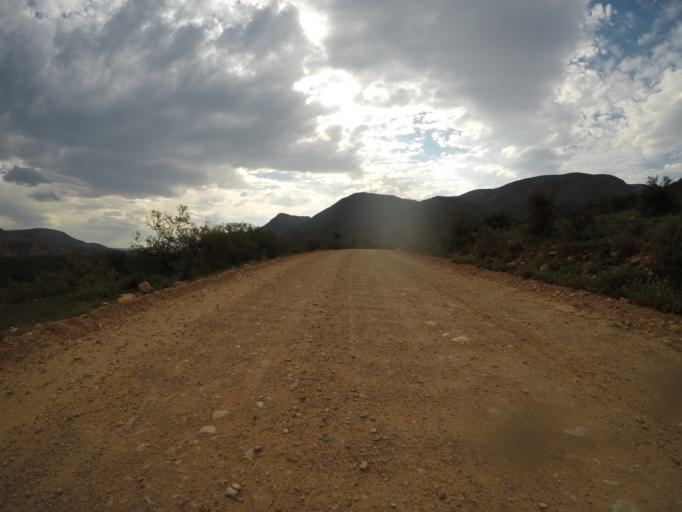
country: ZA
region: Eastern Cape
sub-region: Cacadu District Municipality
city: Kareedouw
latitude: -33.5863
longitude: 24.1656
